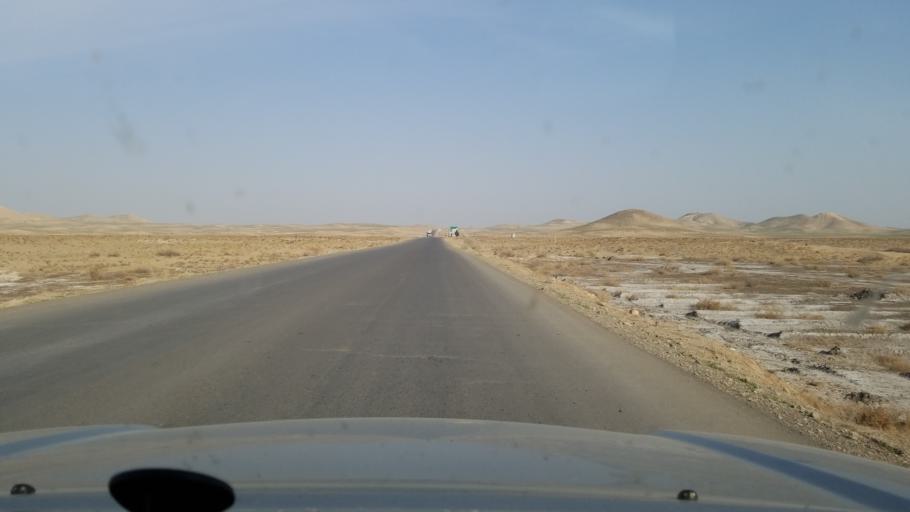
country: AF
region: Jowzjan
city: Khamyab
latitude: 37.6235
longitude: 65.6866
